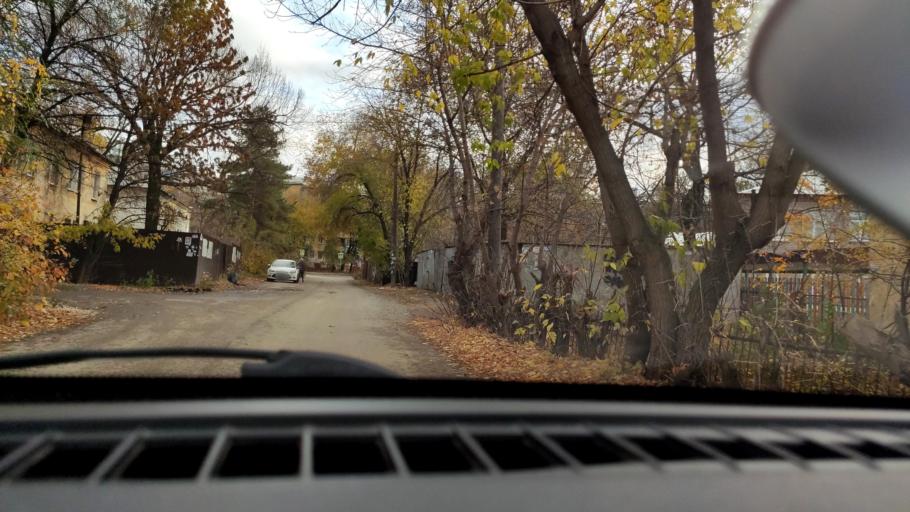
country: RU
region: Samara
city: Samara
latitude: 53.2154
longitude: 50.1969
